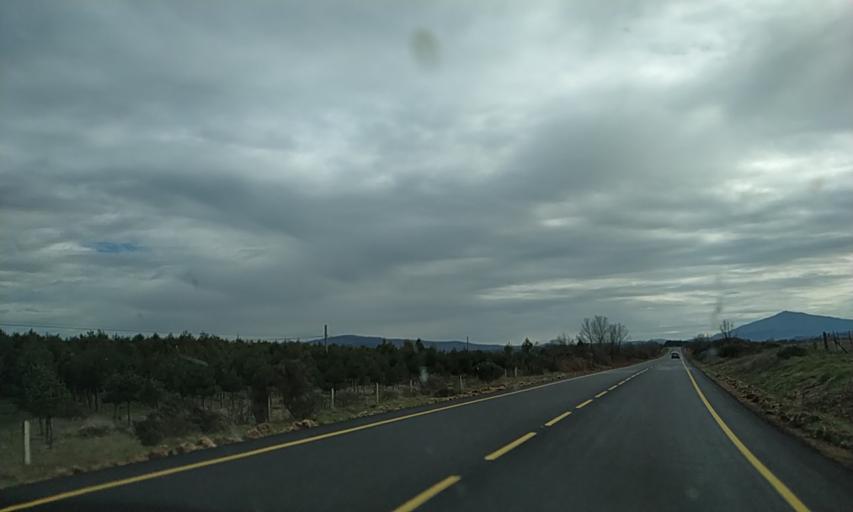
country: ES
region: Castille and Leon
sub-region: Provincia de Salamanca
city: Villasrubias
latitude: 40.3595
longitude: -6.6248
